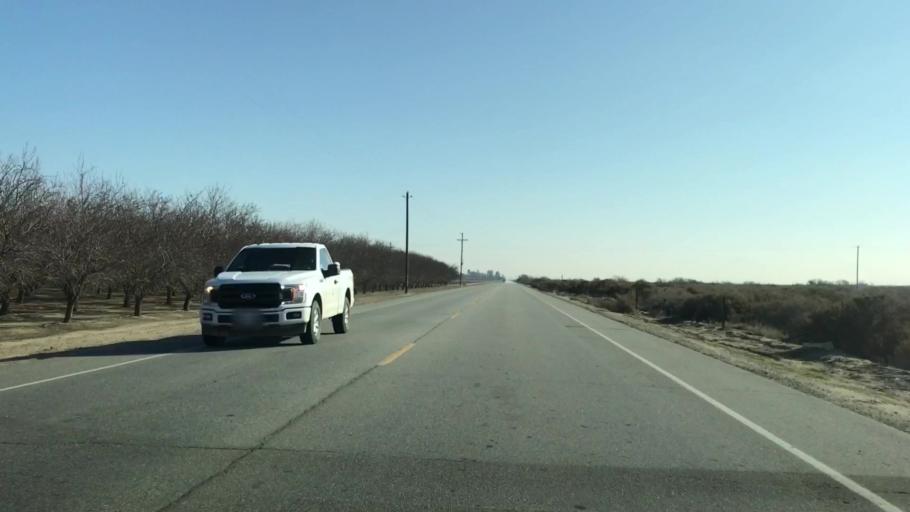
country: US
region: California
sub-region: Kern County
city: Shafter
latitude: 35.3546
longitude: -119.3080
